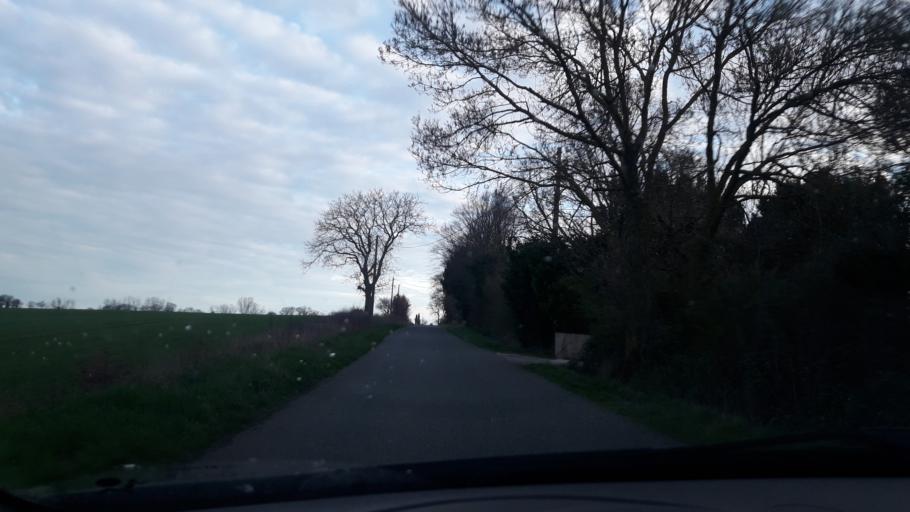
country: FR
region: Midi-Pyrenees
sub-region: Departement du Gers
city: Gimont
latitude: 43.6484
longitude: 1.0046
